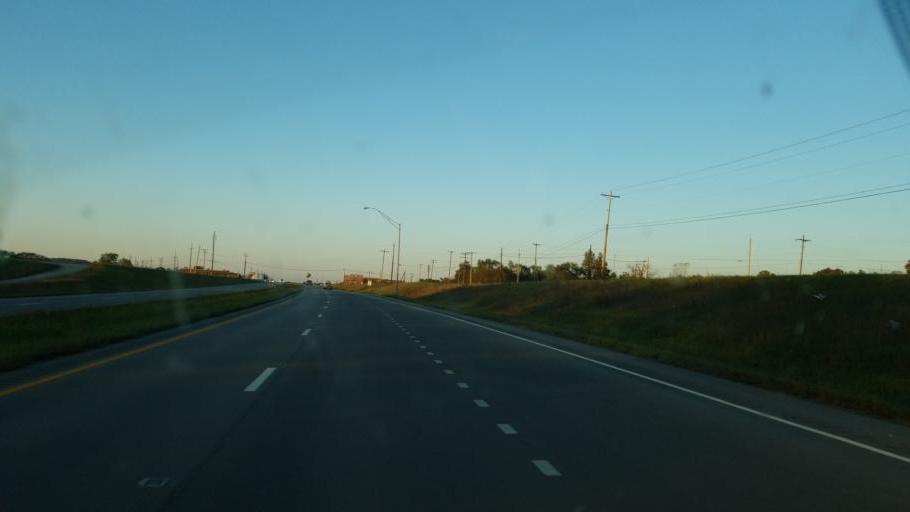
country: US
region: Ohio
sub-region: Pike County
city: Piketon
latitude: 39.0522
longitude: -83.0207
